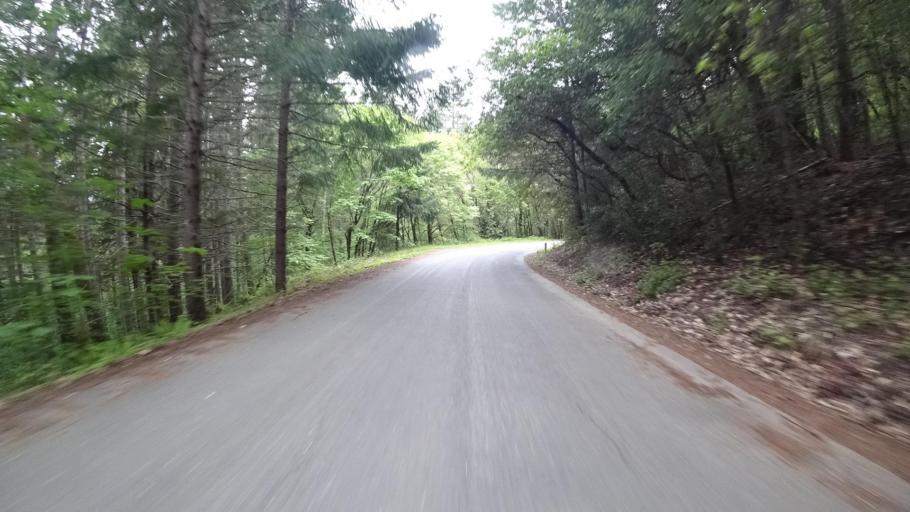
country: US
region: California
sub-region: Humboldt County
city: Willow Creek
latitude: 41.1183
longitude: -123.7249
